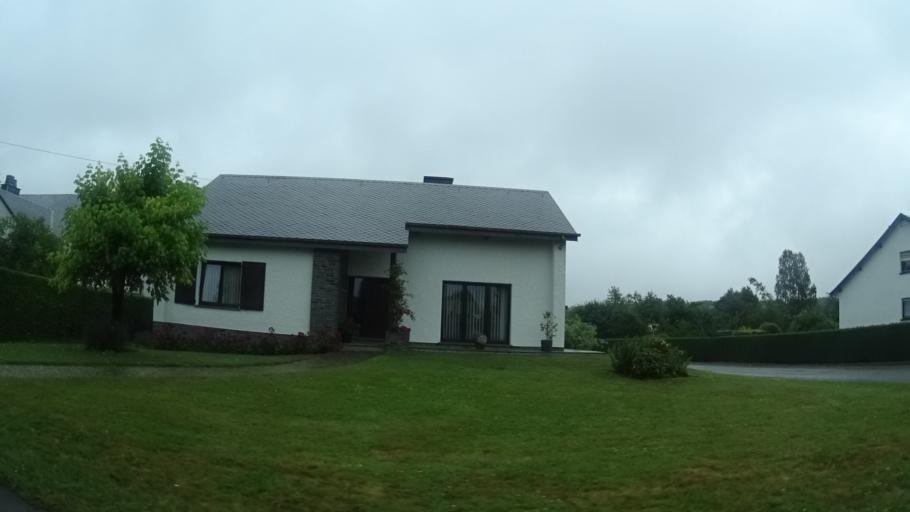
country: BE
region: Wallonia
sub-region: Province du Luxembourg
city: Habay-la-Vieille
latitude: 49.7245
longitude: 5.6498
